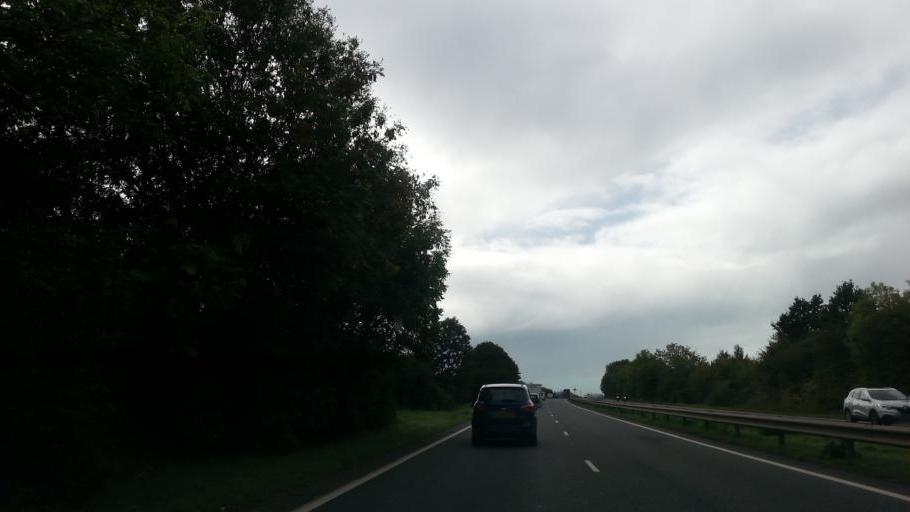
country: GB
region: England
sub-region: Gloucestershire
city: Gloucester
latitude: 51.8296
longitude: -2.2725
